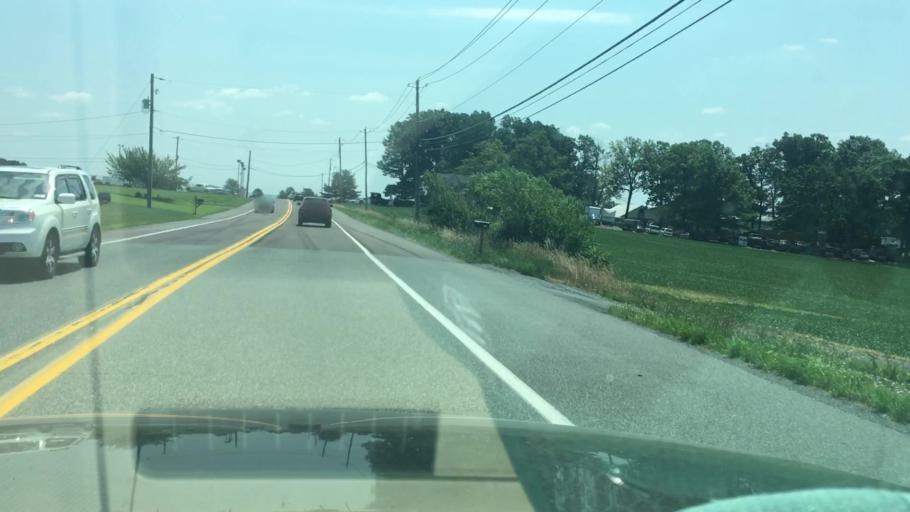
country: US
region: Pennsylvania
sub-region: Lehigh County
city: Schnecksville
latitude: 40.6126
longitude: -75.6516
